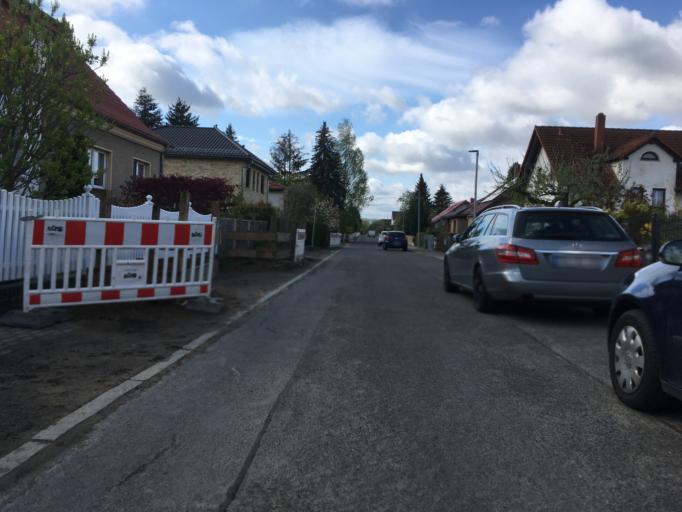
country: DE
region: Berlin
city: Biesdorf
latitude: 52.5204
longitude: 13.5355
